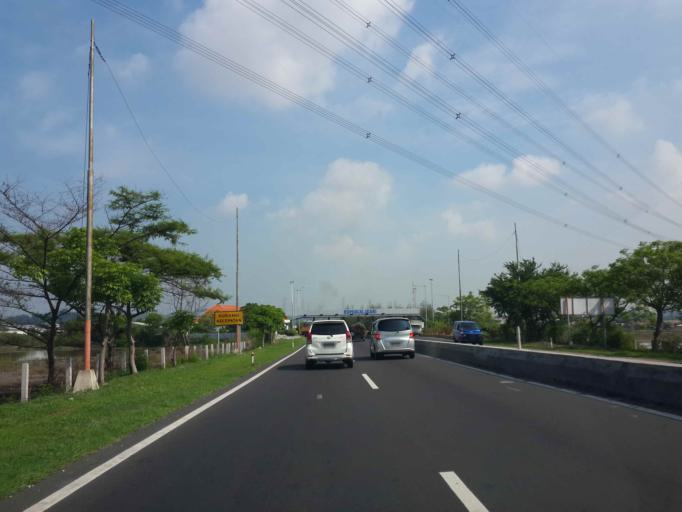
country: ID
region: East Java
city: Kebomas
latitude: -7.2040
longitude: 112.6459
